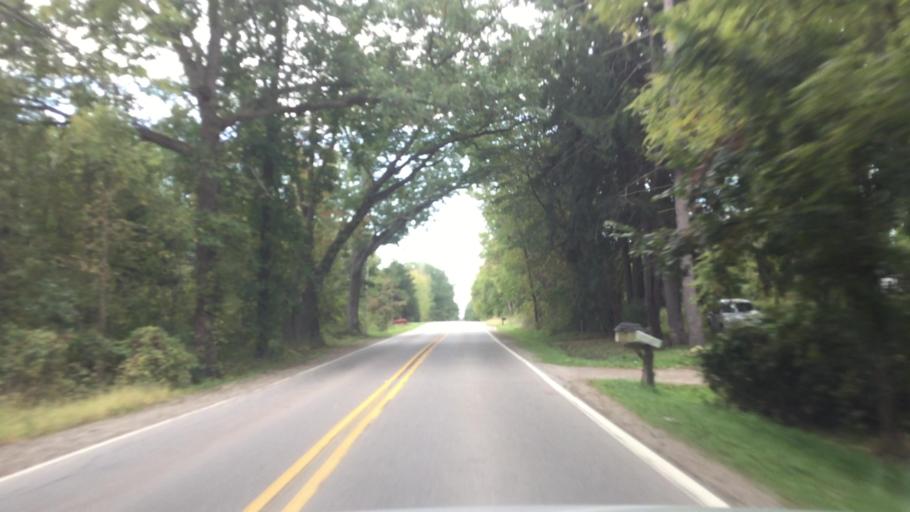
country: US
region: Michigan
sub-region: Genesee County
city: Argentine
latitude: 42.6835
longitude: -83.8383
